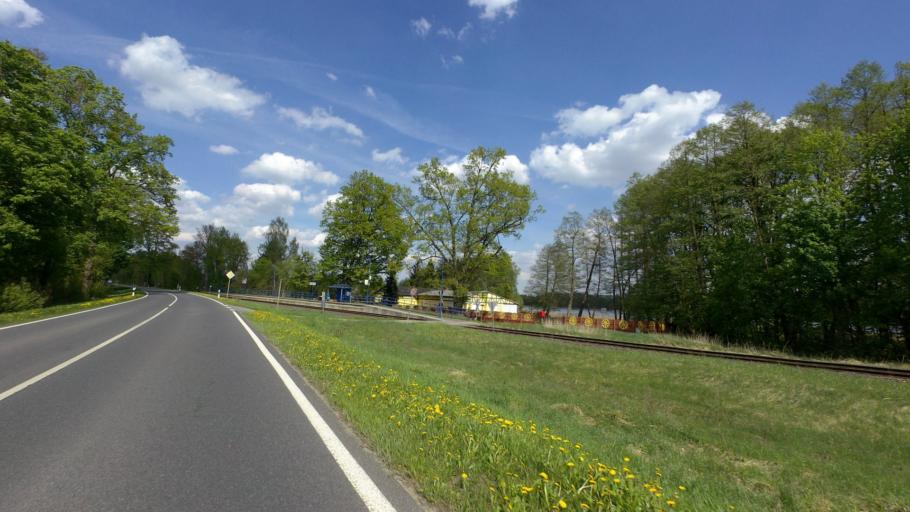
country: DE
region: Brandenburg
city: Wandlitz
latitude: 52.8149
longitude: 13.4984
